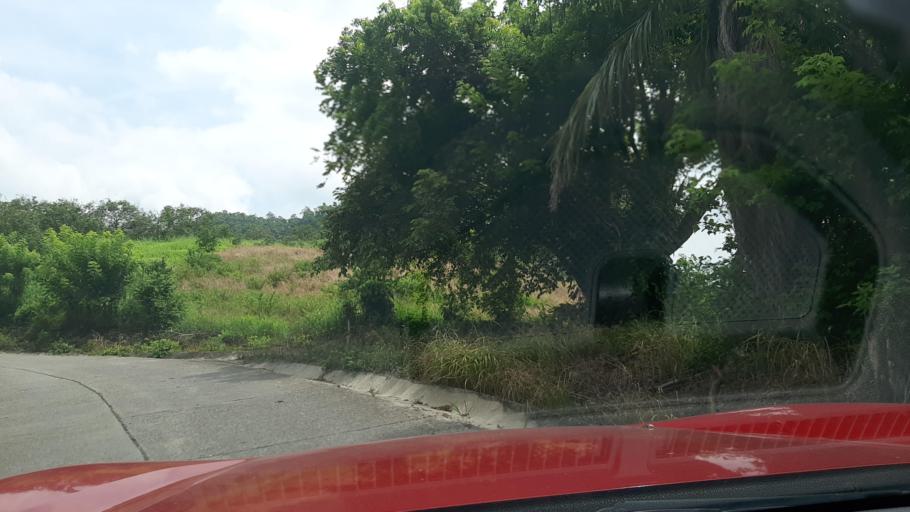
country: MX
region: Veracruz
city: Gutierrez Zamora
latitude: 20.4496
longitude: -97.1764
